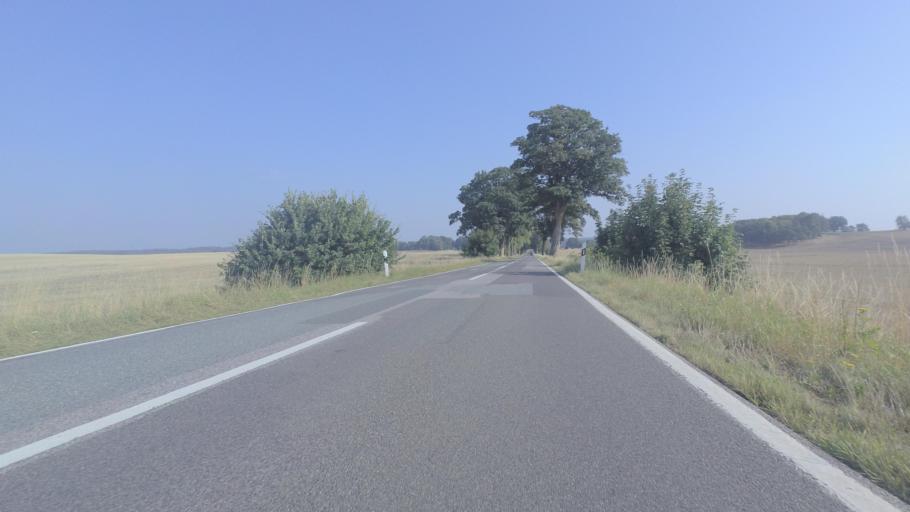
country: DE
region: Mecklenburg-Vorpommern
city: Malchow
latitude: 53.4318
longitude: 12.4333
